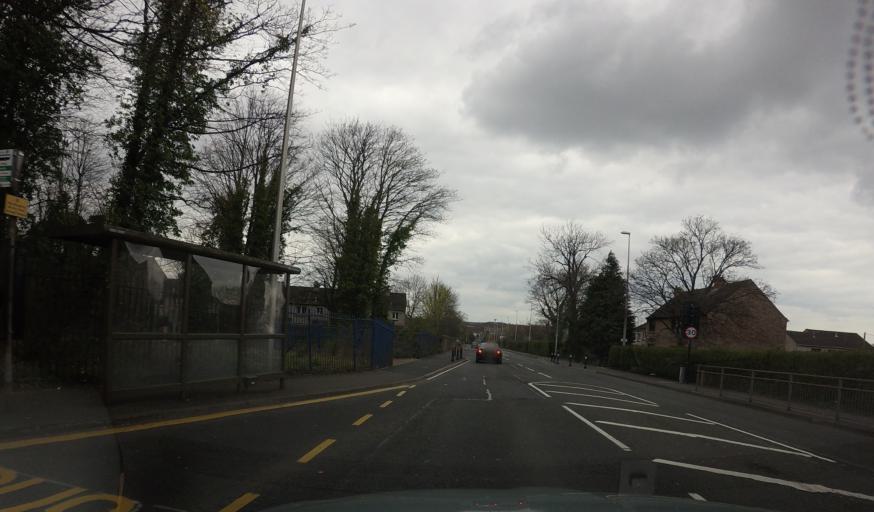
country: GB
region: Scotland
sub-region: Midlothian
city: Dalkeith
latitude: 55.8898
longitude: -3.0547
